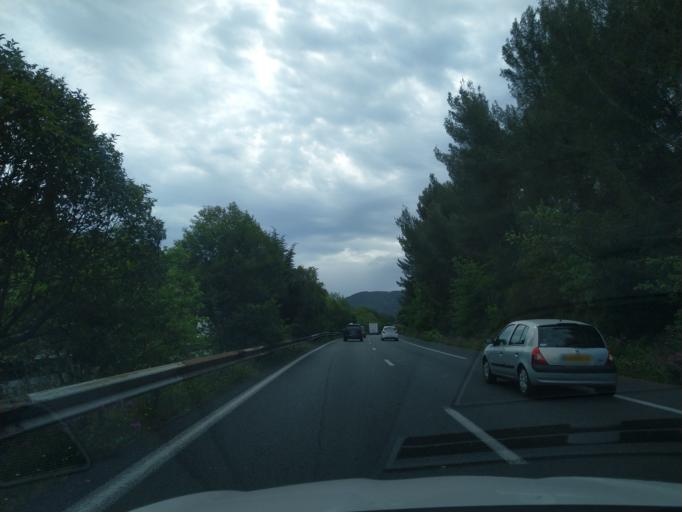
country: FR
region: Provence-Alpes-Cote d'Azur
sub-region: Departement des Bouches-du-Rhone
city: Aubagne
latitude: 43.2865
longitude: 5.5676
